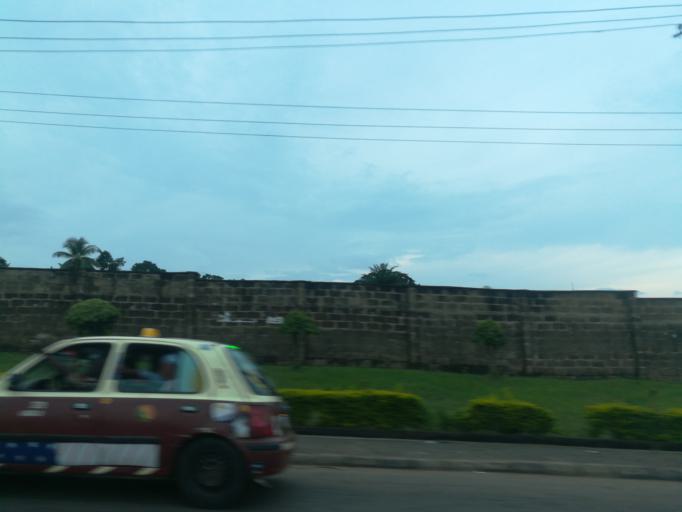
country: NG
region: Oyo
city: Ibadan
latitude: 7.4501
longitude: 3.9067
